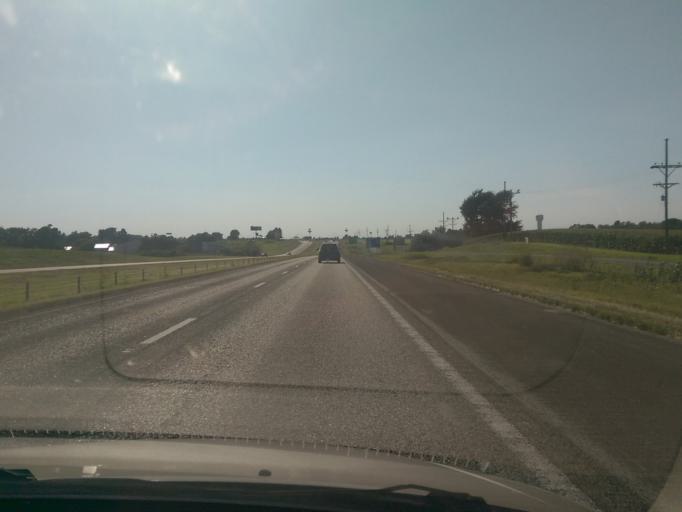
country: US
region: Missouri
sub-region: Lafayette County
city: Concordia
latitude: 38.9903
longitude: -93.5557
